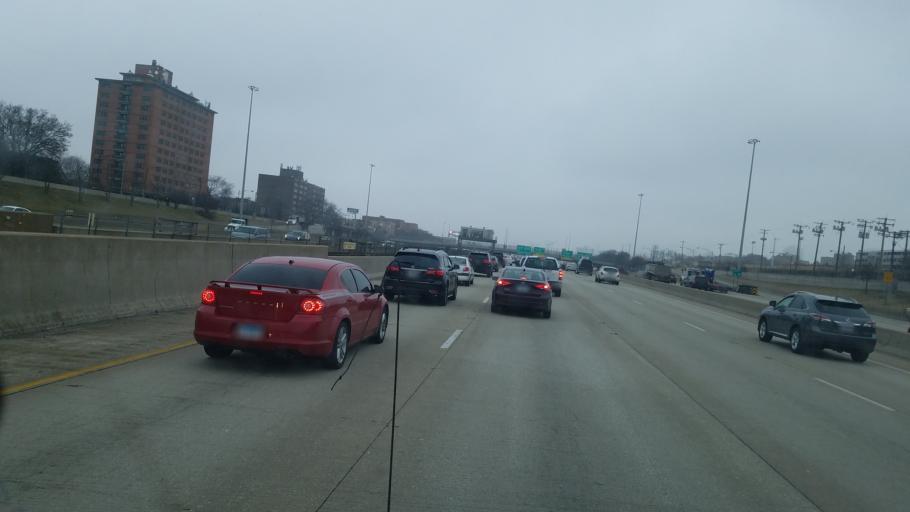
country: US
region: Illinois
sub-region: Cook County
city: Chicago
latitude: 41.8360
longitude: -87.6323
